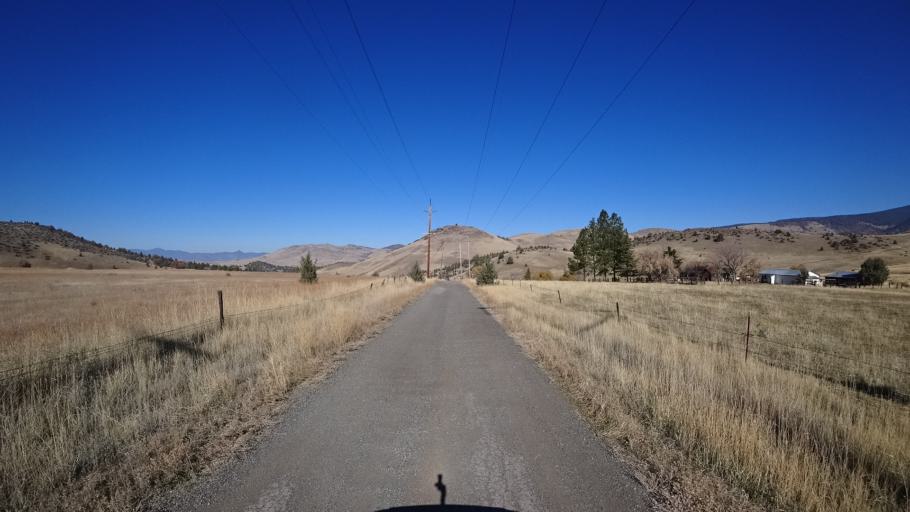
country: US
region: California
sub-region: Siskiyou County
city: Montague
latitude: 41.7831
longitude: -122.3591
